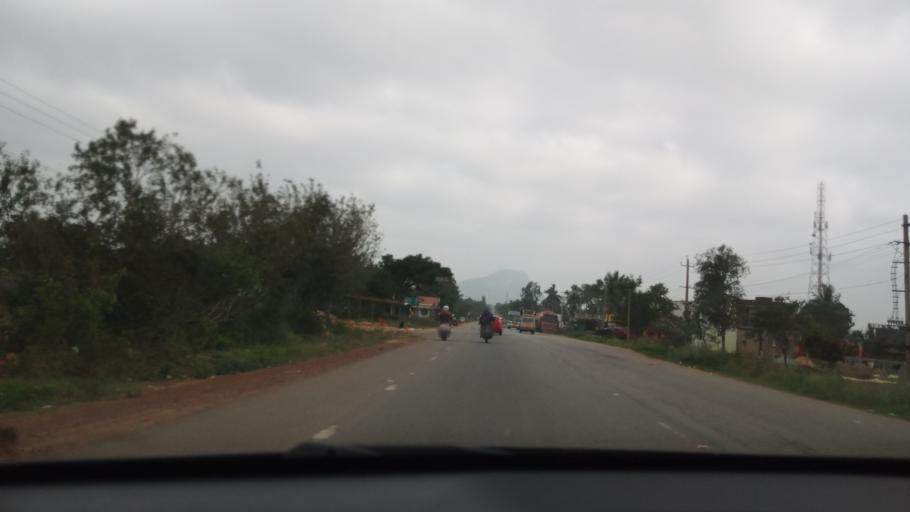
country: IN
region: Karnataka
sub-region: Chikkaballapur
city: Chintamani
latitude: 13.3036
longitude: 77.9725
